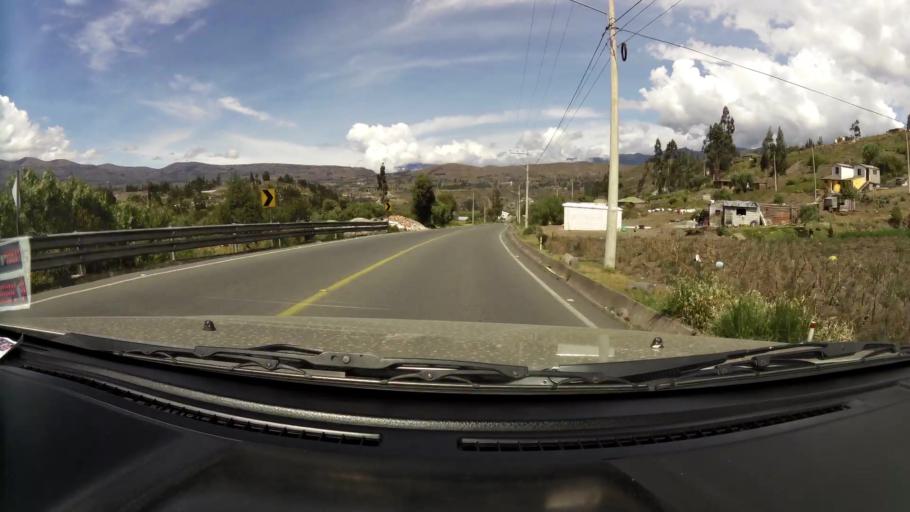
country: EC
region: Chimborazo
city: Guano
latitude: -1.6403
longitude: -78.6039
